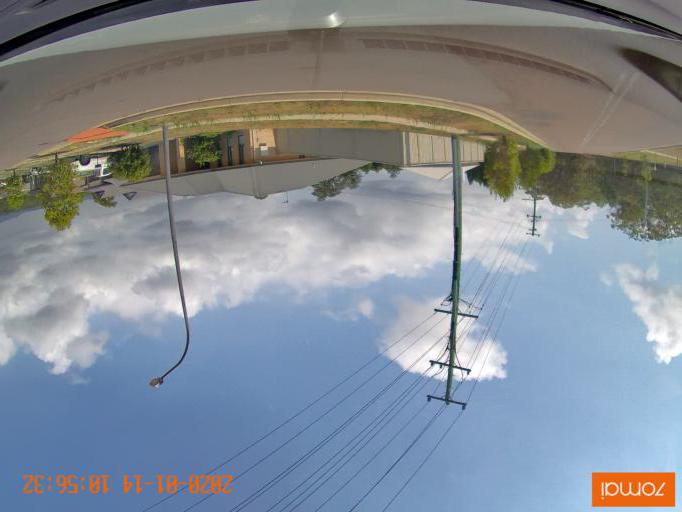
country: AU
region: New South Wales
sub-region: Lake Macquarie Shire
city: Dora Creek
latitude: -33.1001
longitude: 151.4873
